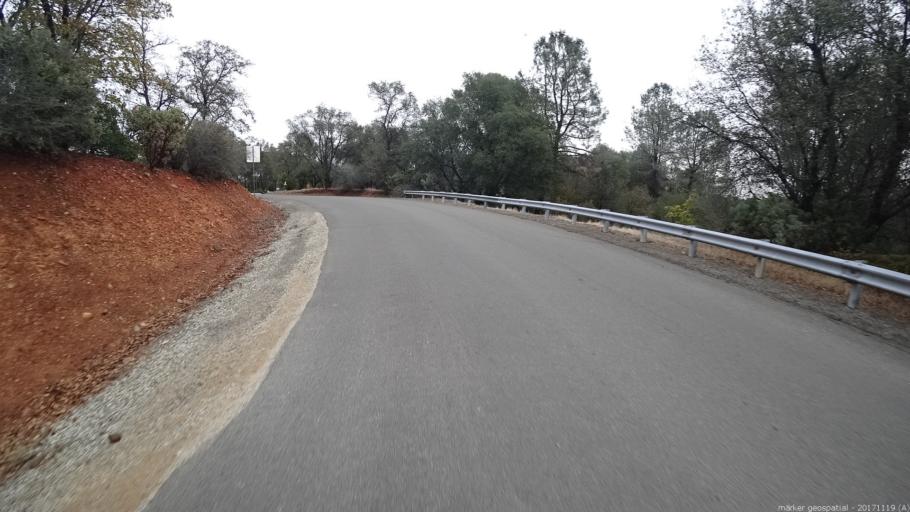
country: US
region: California
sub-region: Shasta County
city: Redding
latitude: 40.4928
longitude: -122.4061
